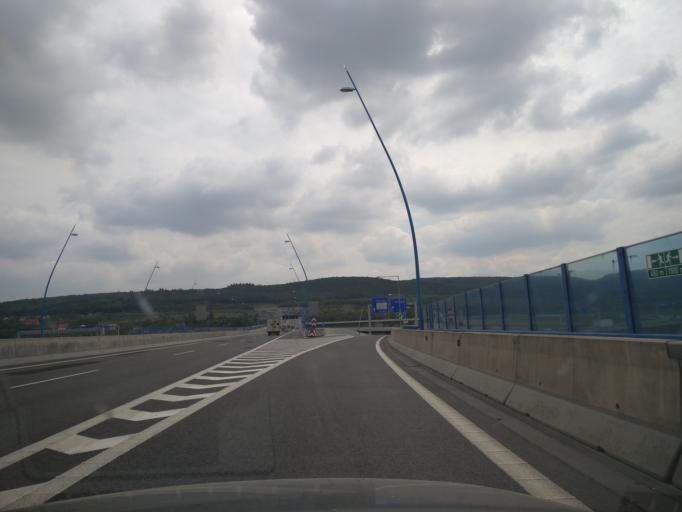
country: CZ
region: Praha
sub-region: Praha 12
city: Modrany
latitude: 49.9873
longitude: 14.3910
